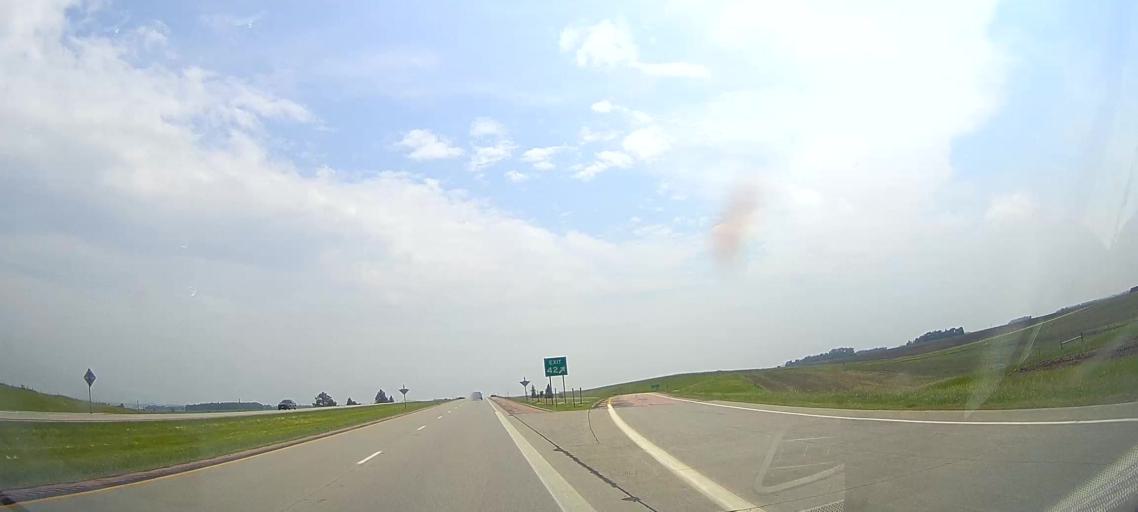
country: US
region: South Dakota
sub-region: Union County
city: Beresford
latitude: 43.0137
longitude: -96.7959
